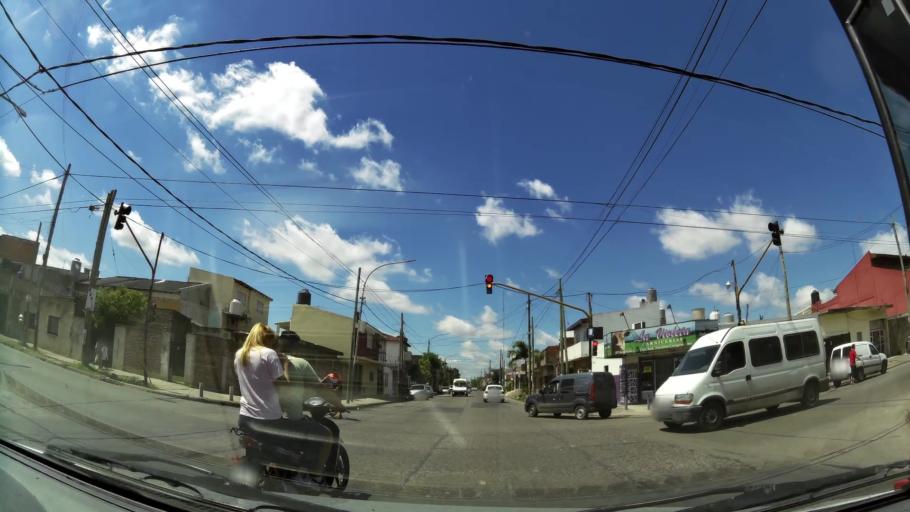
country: AR
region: Buenos Aires
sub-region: Partido de Lanus
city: Lanus
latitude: -34.6954
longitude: -58.4231
